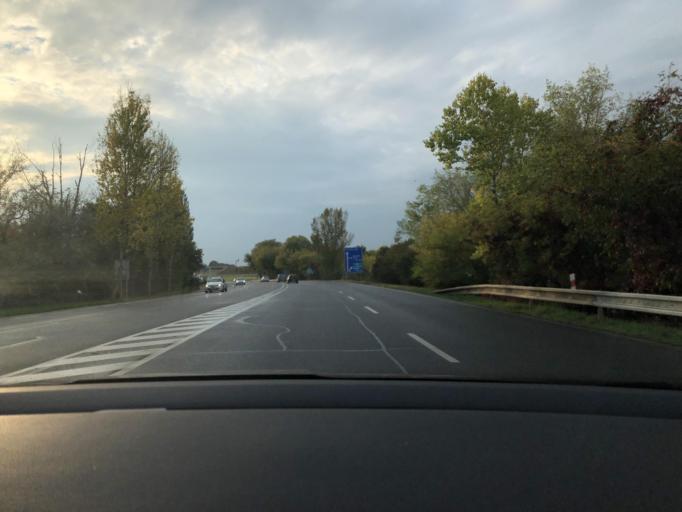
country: CZ
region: Central Bohemia
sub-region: Okres Kolin
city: Kolin
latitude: 50.0329
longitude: 15.1765
